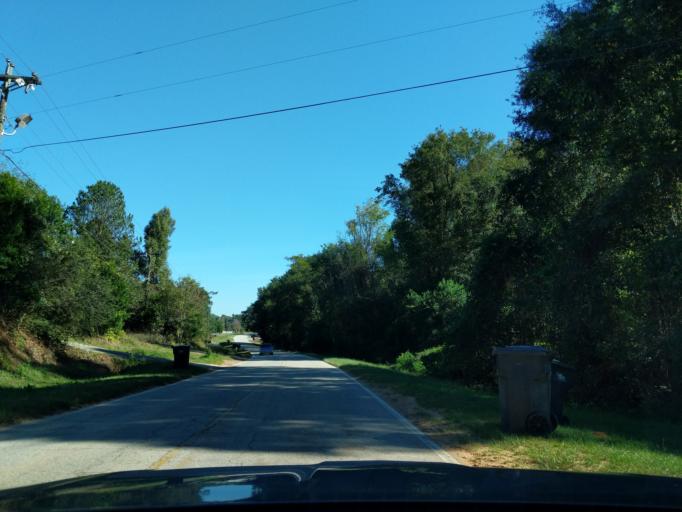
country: US
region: Georgia
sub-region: Richmond County
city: Hephzibah
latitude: 33.2578
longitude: -81.9999
